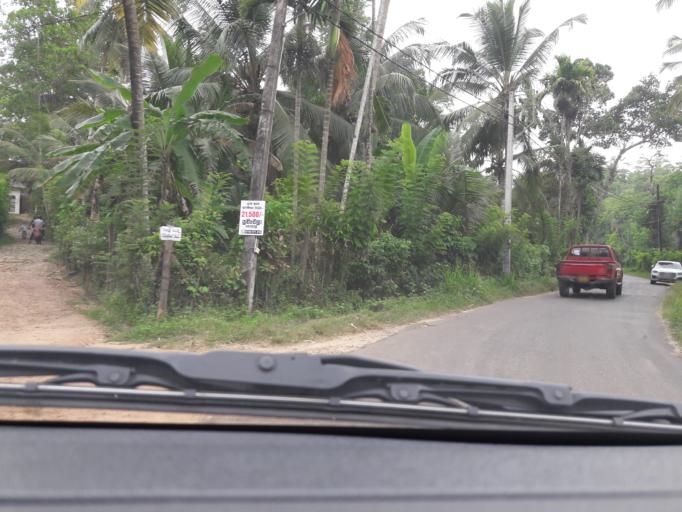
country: LK
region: Southern
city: Unawatuna
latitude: 6.0611
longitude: 80.2510
